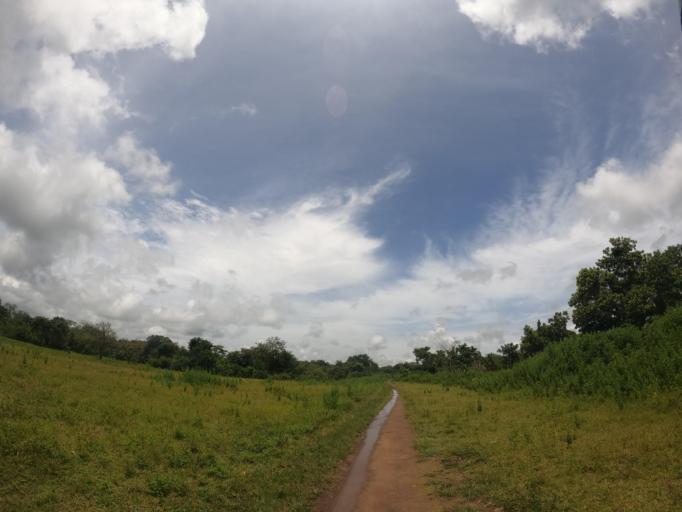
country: SL
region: Northern Province
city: Binkolo
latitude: 9.1367
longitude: -12.2375
